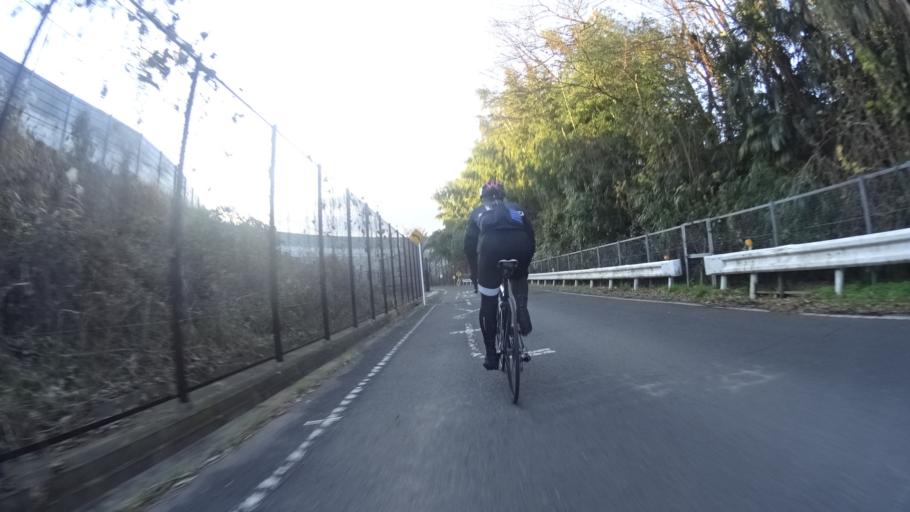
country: JP
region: Kanagawa
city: Zama
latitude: 35.4778
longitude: 139.3715
